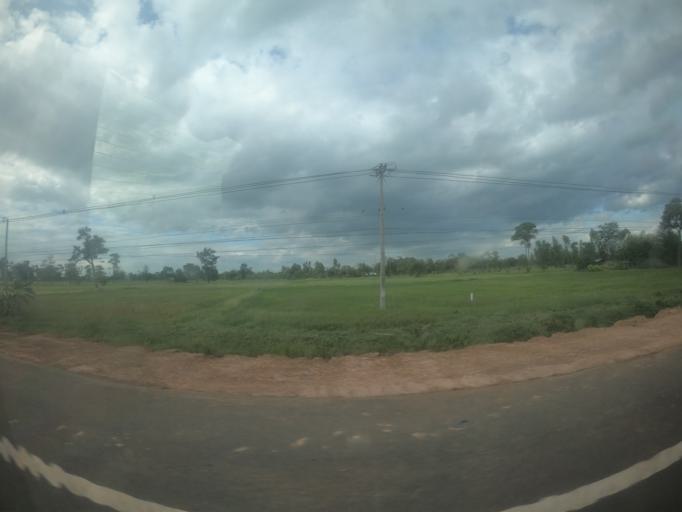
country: TH
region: Surin
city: Kap Choeng
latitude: 14.5195
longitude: 103.5430
